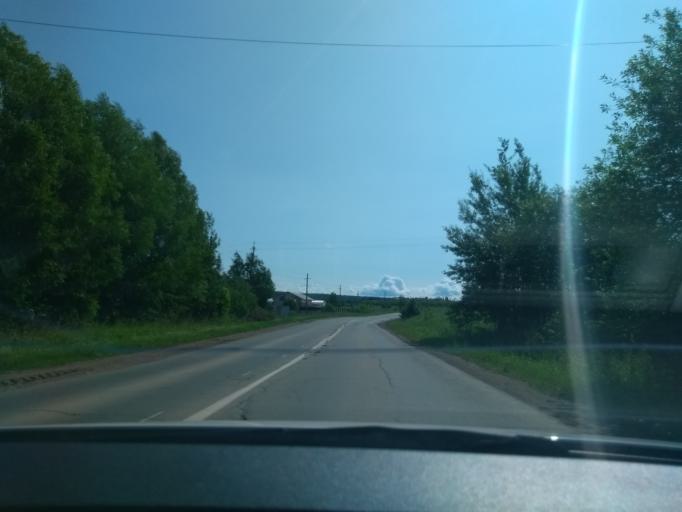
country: RU
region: Perm
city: Lobanovo
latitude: 57.8550
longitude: 56.3190
